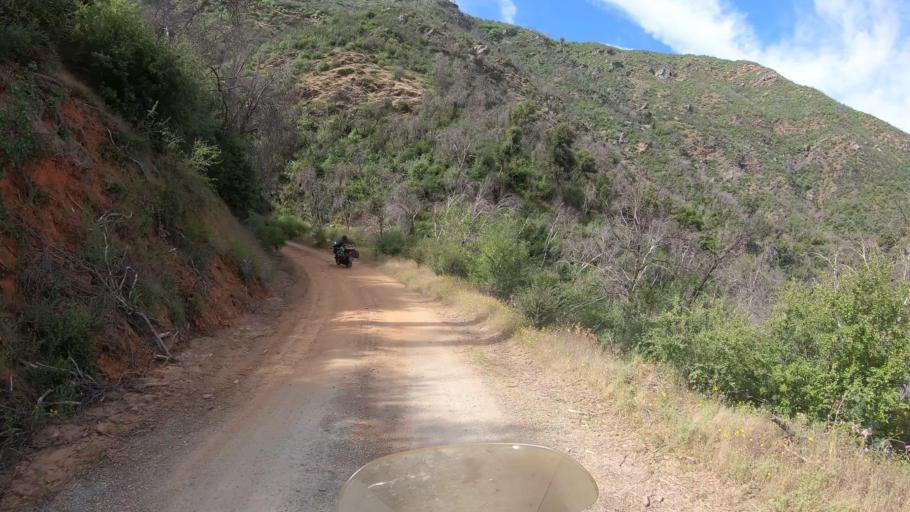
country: US
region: California
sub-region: Tuolumne County
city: Tuolumne City
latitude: 37.8362
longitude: -120.0628
